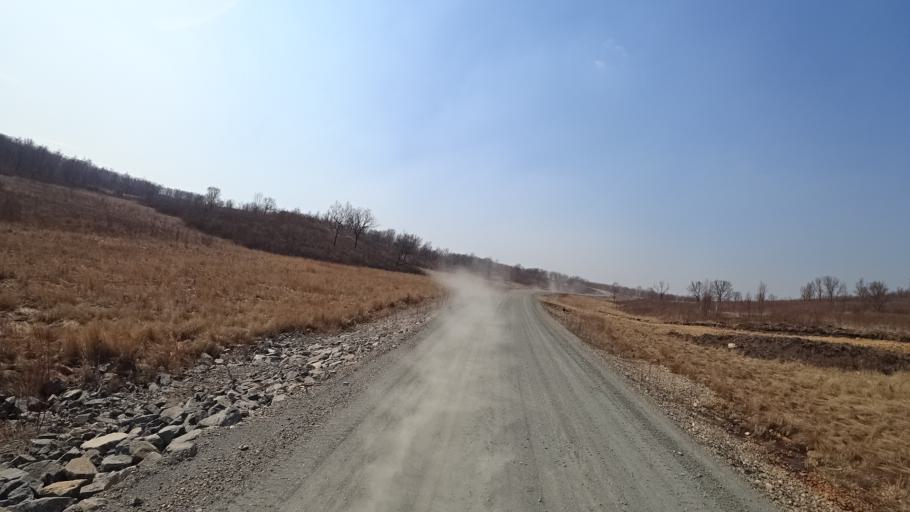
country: RU
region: Amur
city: Novobureyskiy
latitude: 49.8222
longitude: 129.9992
